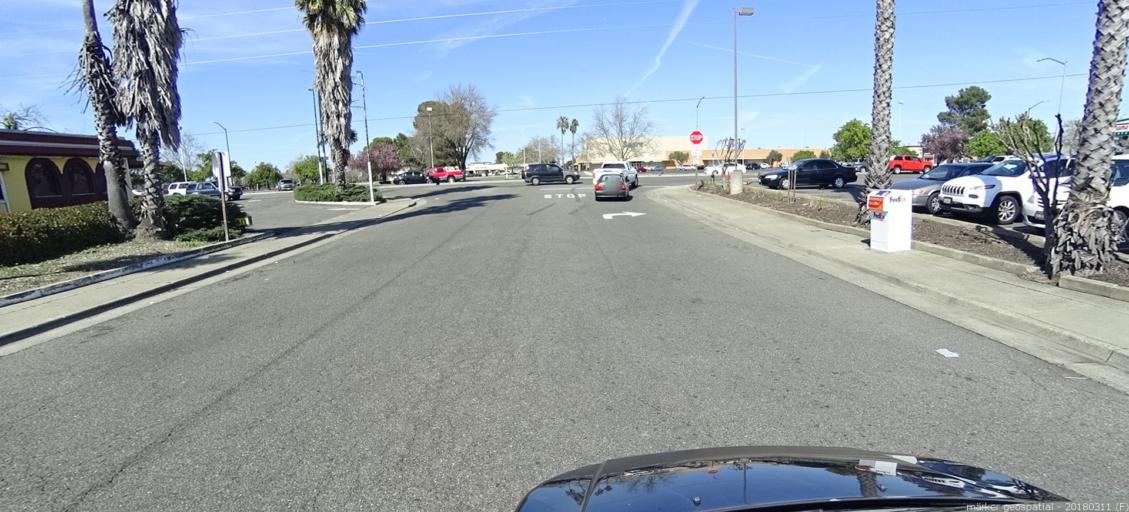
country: US
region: California
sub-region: Sacramento County
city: Parkway
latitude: 38.4956
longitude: -121.4368
